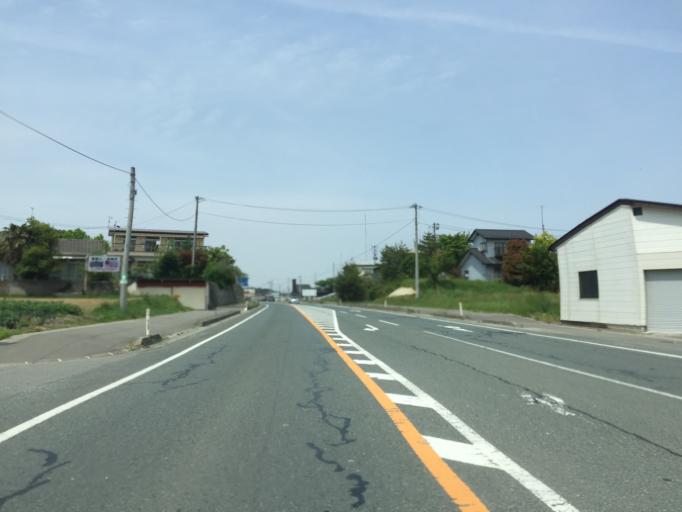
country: JP
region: Miyagi
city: Marumori
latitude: 37.8728
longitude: 140.9193
